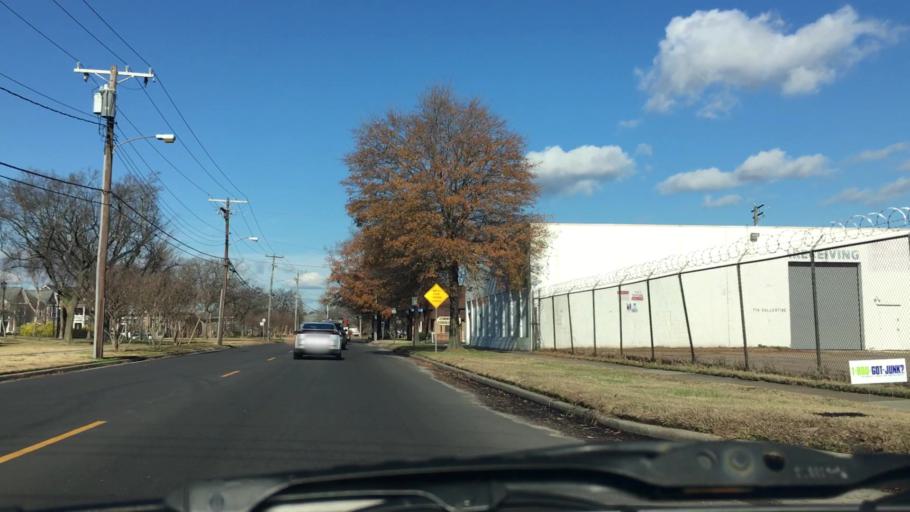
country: US
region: Virginia
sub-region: City of Norfolk
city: Norfolk
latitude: 36.8545
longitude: -76.2485
